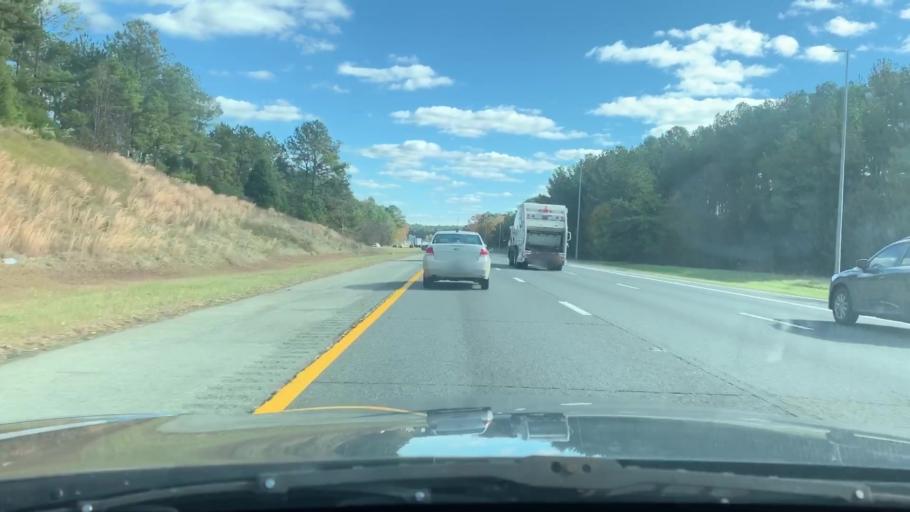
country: US
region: North Carolina
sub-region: Wake County
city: Morrisville
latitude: 35.8992
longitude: -78.8719
